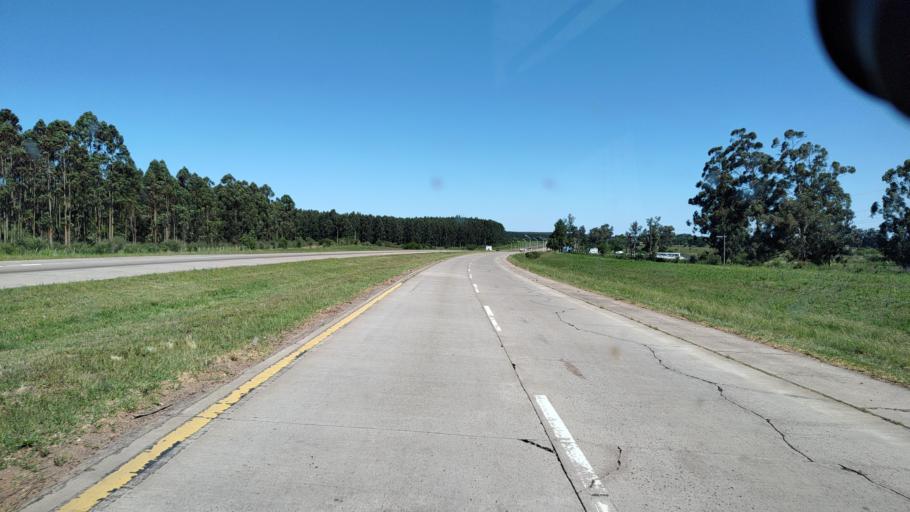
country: AR
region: Entre Rios
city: Villa Elisa
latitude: -32.0795
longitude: -58.2517
